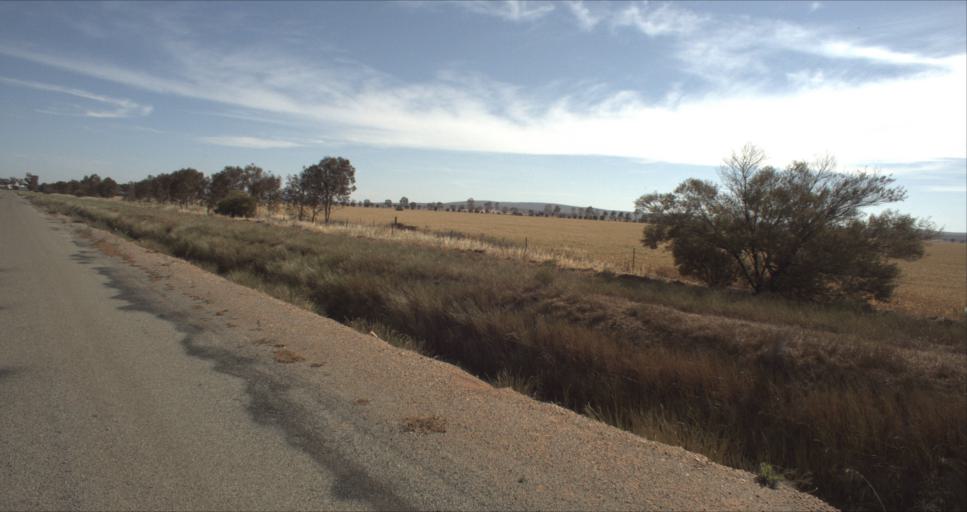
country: AU
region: New South Wales
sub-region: Leeton
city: Leeton
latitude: -34.5662
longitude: 146.4717
